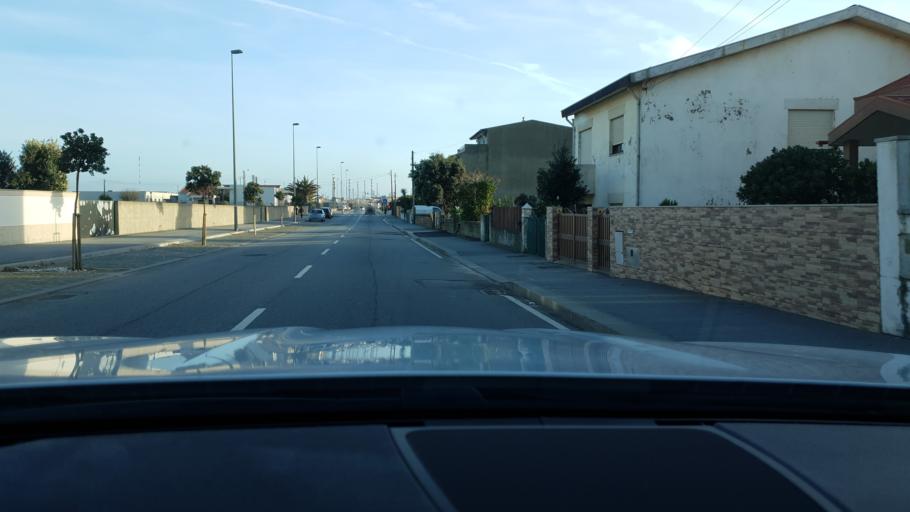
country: PT
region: Porto
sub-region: Matosinhos
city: Lavra
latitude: 41.2361
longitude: -8.7216
